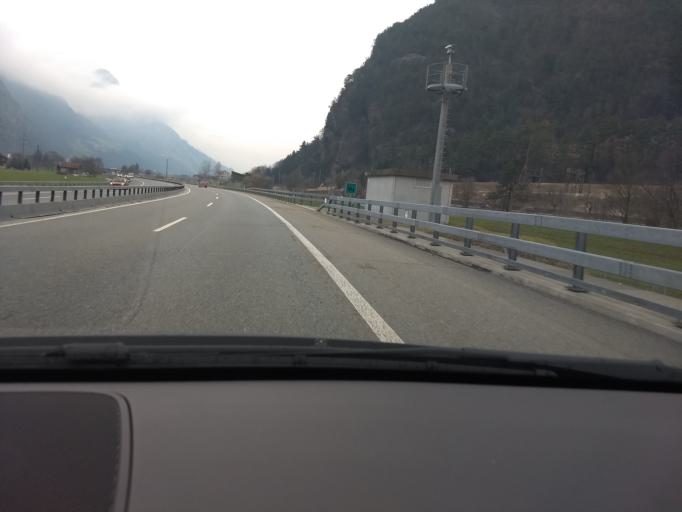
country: CH
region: Uri
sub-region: Uri
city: Erstfeld
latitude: 46.8092
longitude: 8.6600
